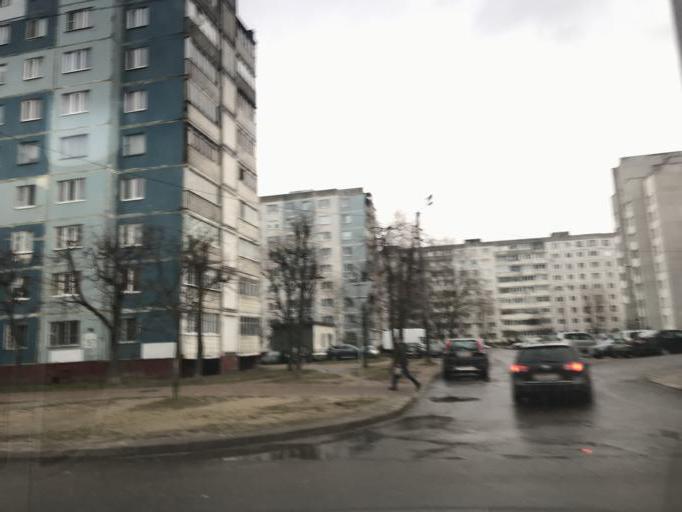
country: BY
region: Mogilev
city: Mahilyow
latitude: 53.8713
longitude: 30.3371
